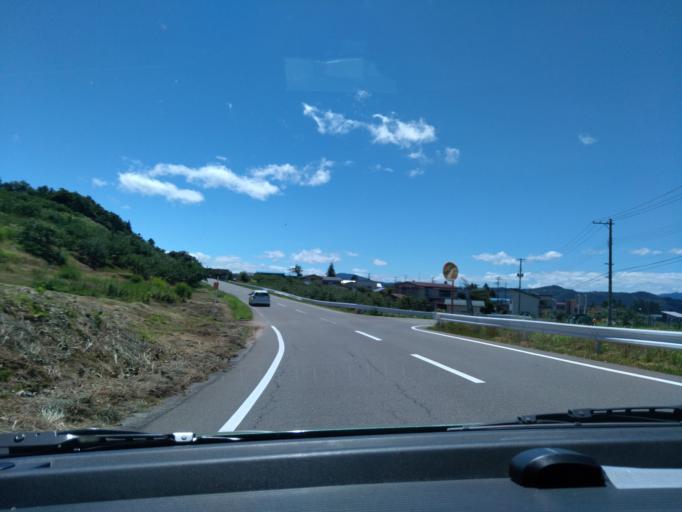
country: JP
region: Akita
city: Yokotemachi
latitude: 39.2318
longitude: 140.5646
